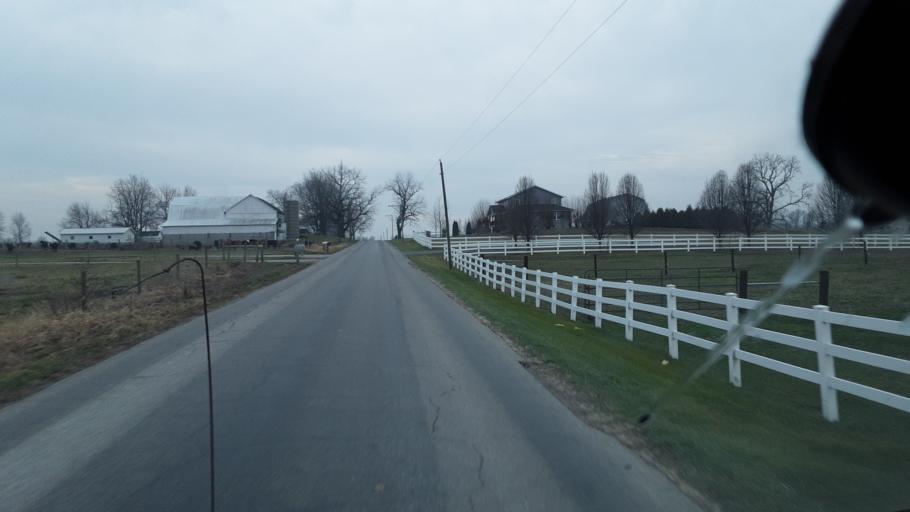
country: US
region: Indiana
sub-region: Elkhart County
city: Middlebury
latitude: 41.6851
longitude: -85.6198
